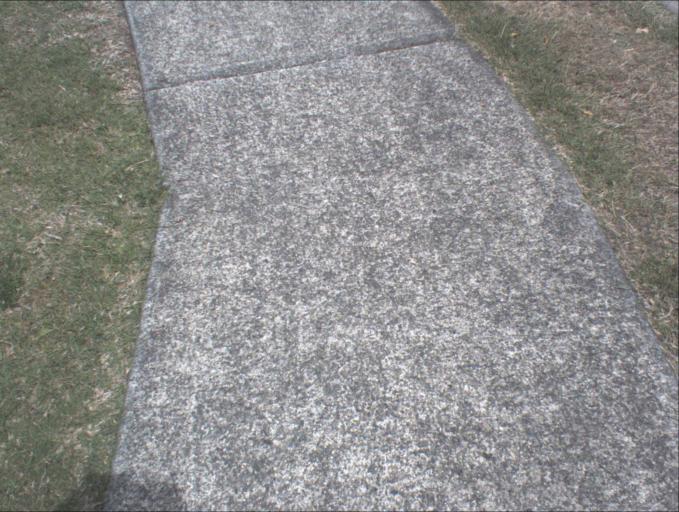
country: AU
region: Queensland
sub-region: Logan
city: Springwood
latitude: -27.6148
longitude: 153.1109
